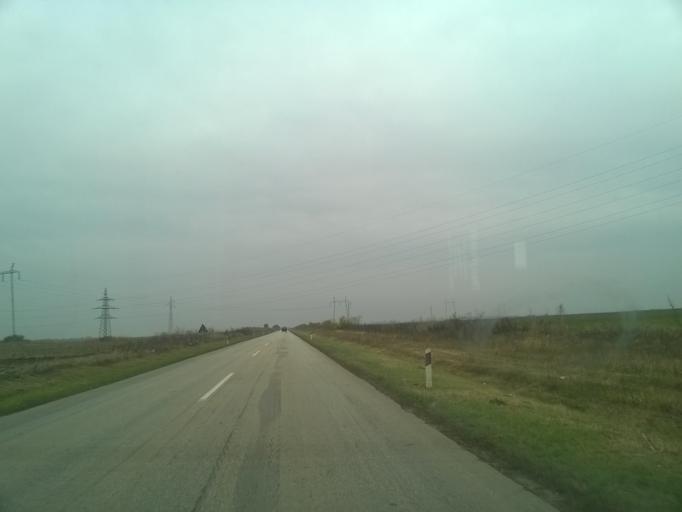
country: RS
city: Crepaja
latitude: 44.9643
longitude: 20.6546
